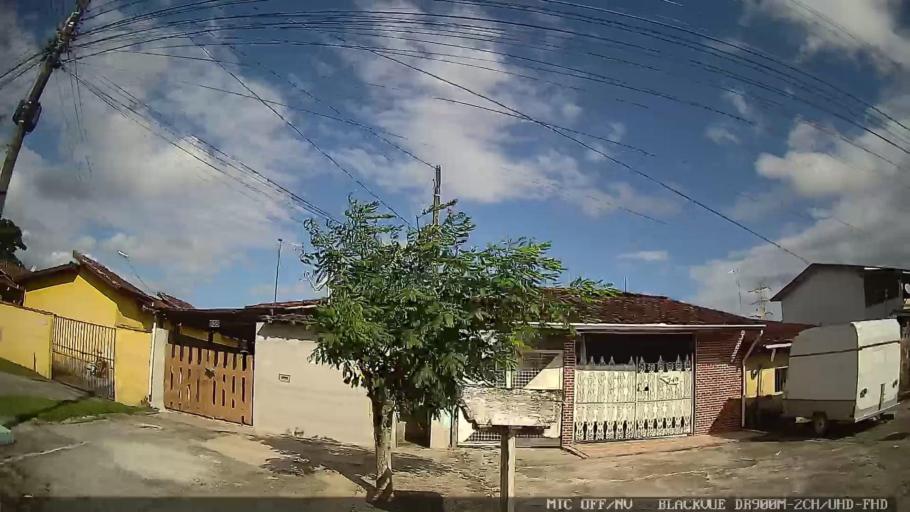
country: BR
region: Sao Paulo
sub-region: Caraguatatuba
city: Caraguatatuba
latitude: -23.6363
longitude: -45.4383
